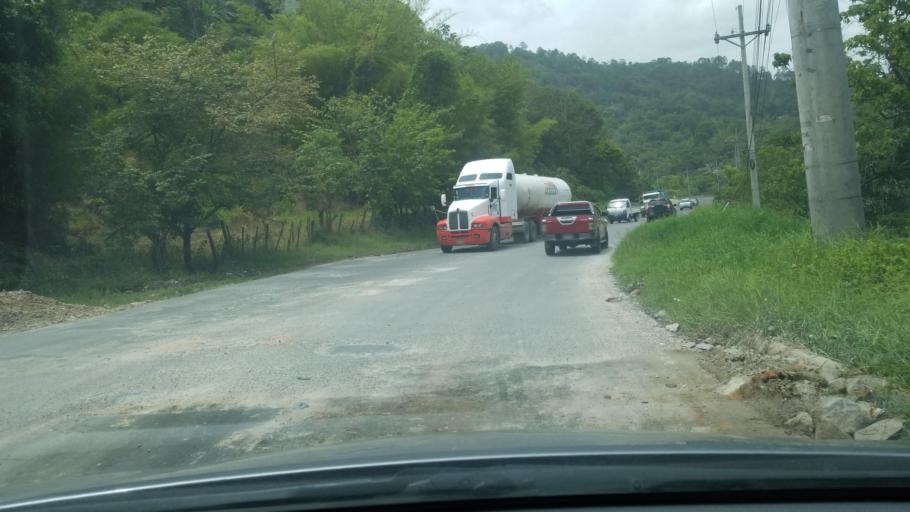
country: HN
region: Copan
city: Santa Rosa de Copan
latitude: 14.7535
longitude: -88.7767
